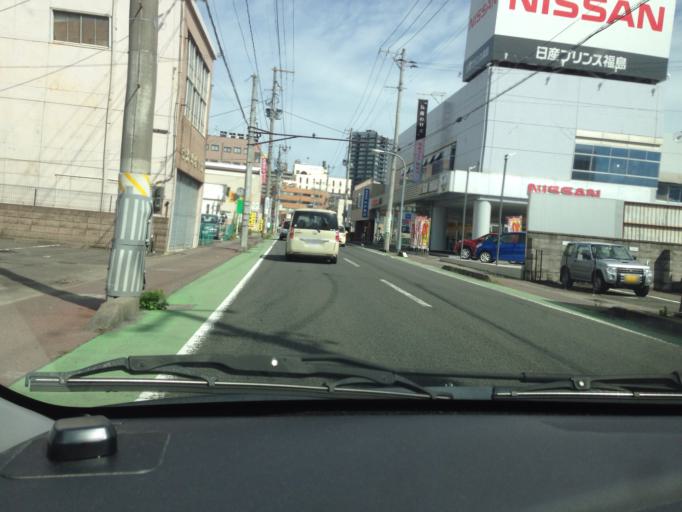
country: JP
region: Fukushima
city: Fukushima-shi
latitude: 37.7473
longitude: 140.4645
